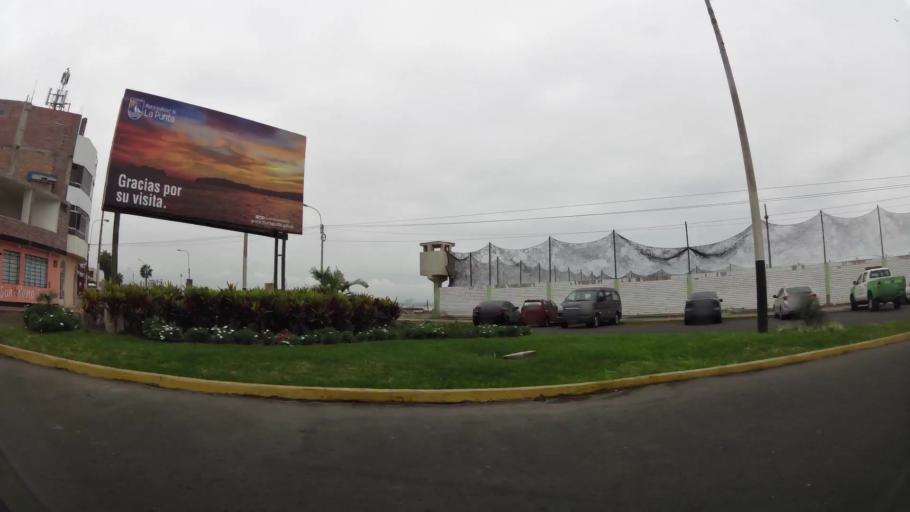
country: PE
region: Callao
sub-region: Callao
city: Callao
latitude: -12.0684
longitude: -77.1575
